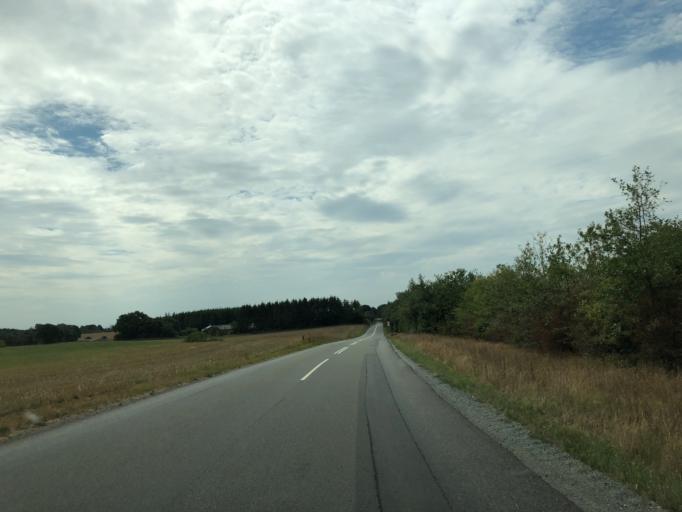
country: DK
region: South Denmark
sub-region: Vejle Kommune
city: Egtved
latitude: 55.6208
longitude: 9.1930
